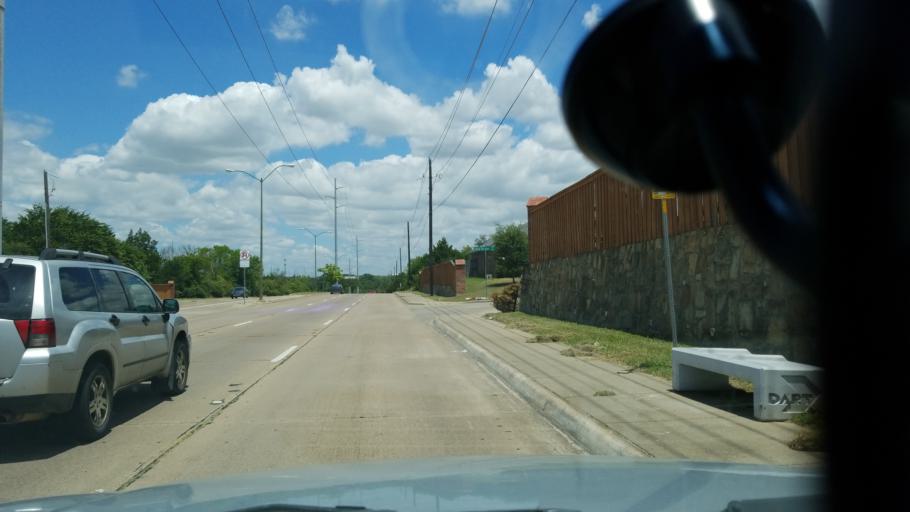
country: US
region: Texas
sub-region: Dallas County
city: Duncanville
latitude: 32.6667
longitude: -96.8816
